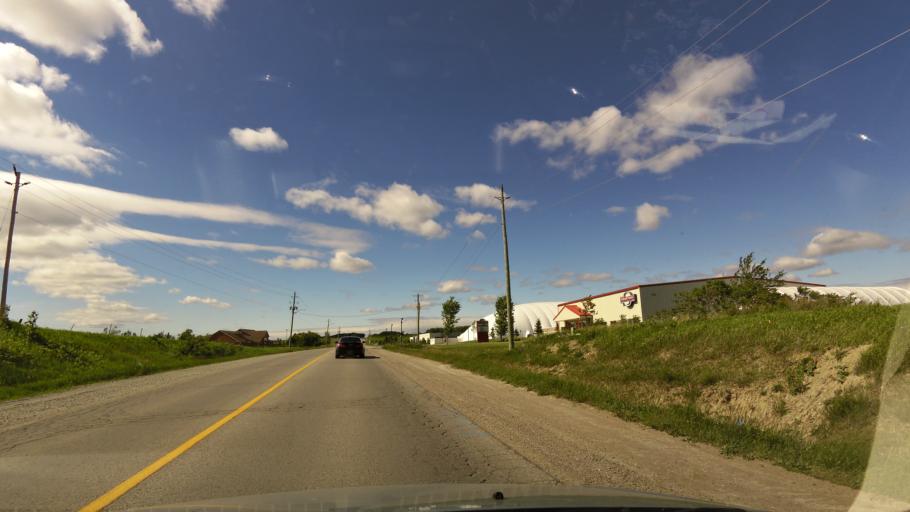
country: CA
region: Ontario
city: Bradford West Gwillimbury
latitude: 44.1143
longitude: -79.6041
